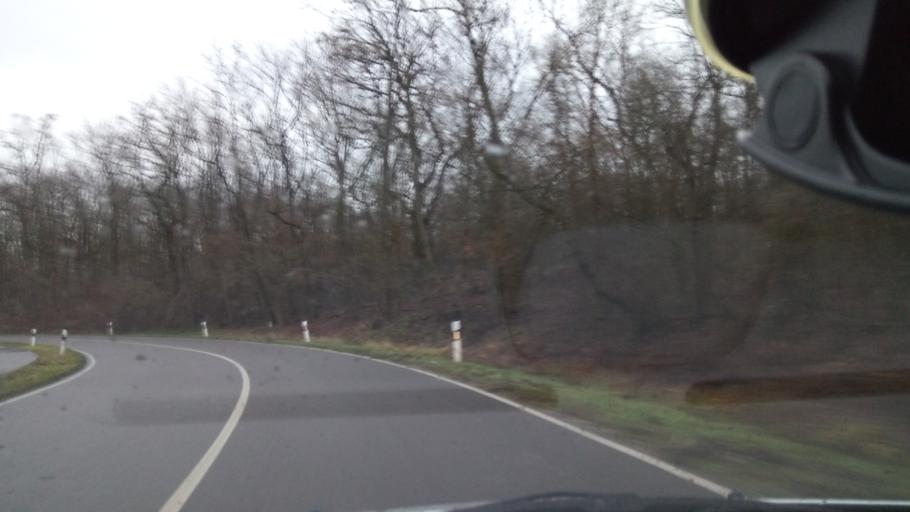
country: DE
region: Saxony-Anhalt
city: Muldenstein
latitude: 51.6596
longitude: 12.3450
